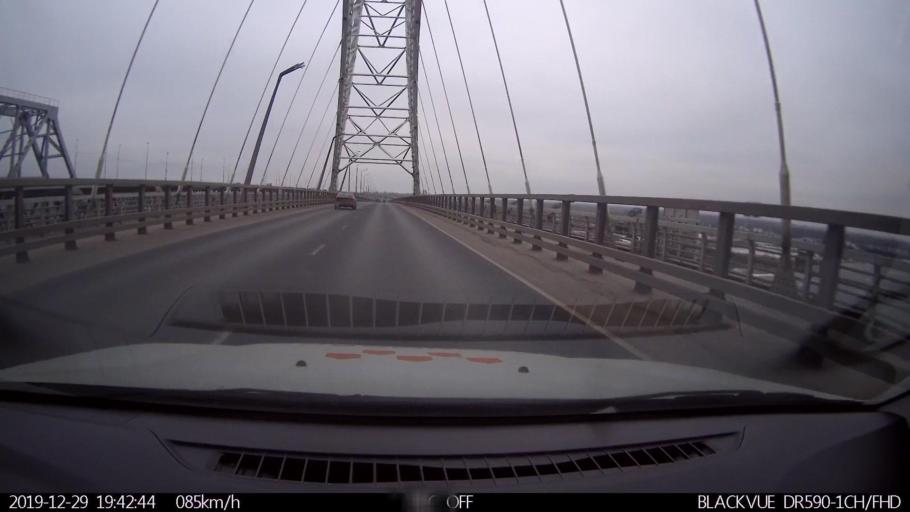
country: RU
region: Nizjnij Novgorod
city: Neklyudovo
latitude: 56.3533
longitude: 43.9251
